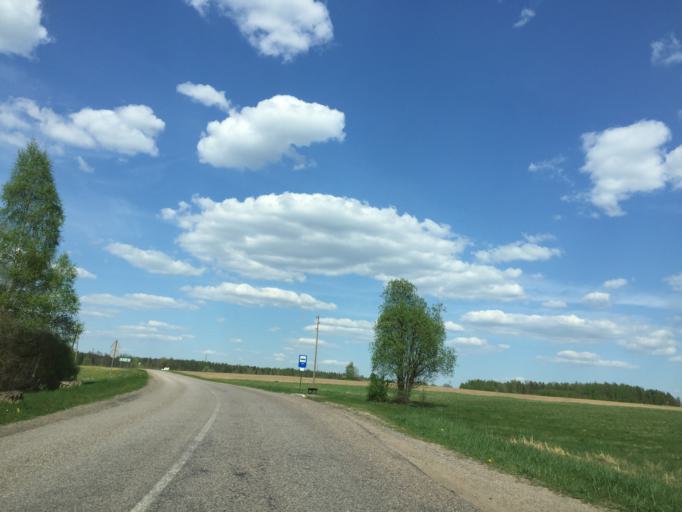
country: LV
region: Limbazu Rajons
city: Limbazi
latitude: 57.3824
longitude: 24.6853
